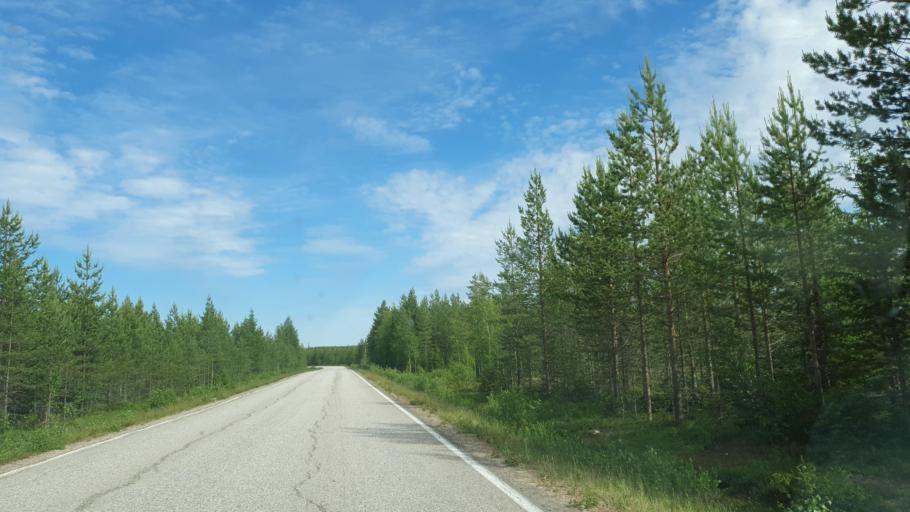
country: FI
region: Kainuu
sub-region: Kehys-Kainuu
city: Suomussalmi
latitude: 64.5738
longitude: 29.0143
